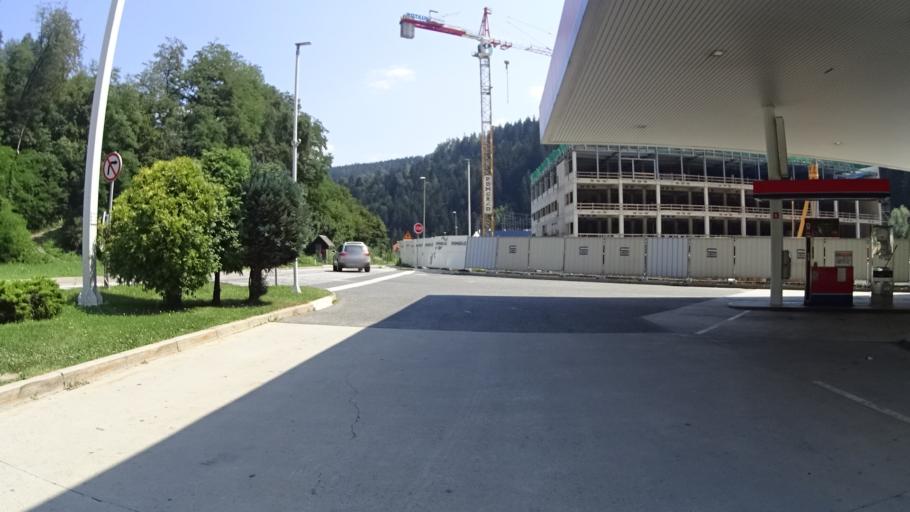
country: SI
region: Prevalje
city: Prevalje
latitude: 46.5428
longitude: 14.9040
